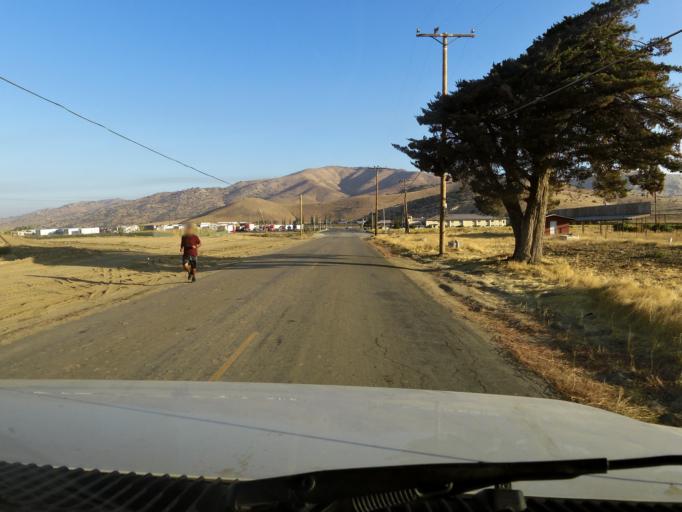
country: US
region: California
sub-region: Kern County
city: Tehachapi
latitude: 35.1234
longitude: -118.4143
